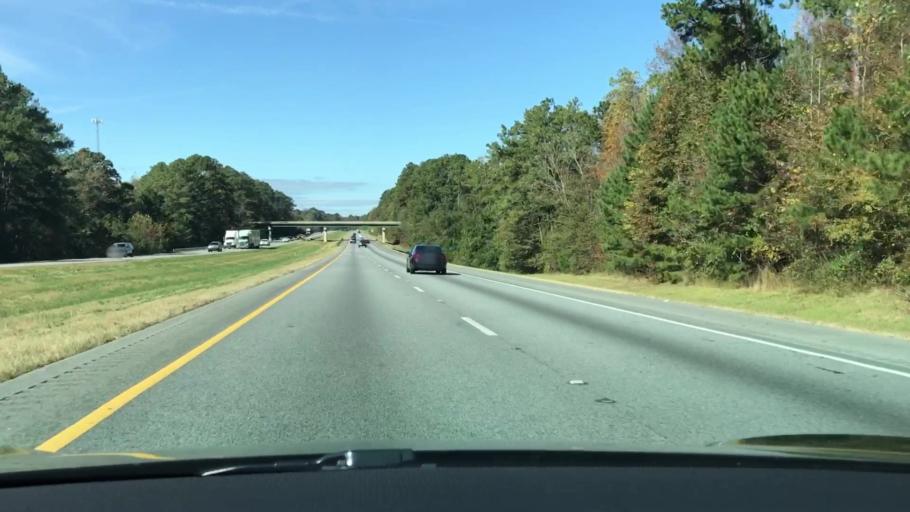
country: US
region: Georgia
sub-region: Morgan County
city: Madison
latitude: 33.5719
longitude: -83.5219
